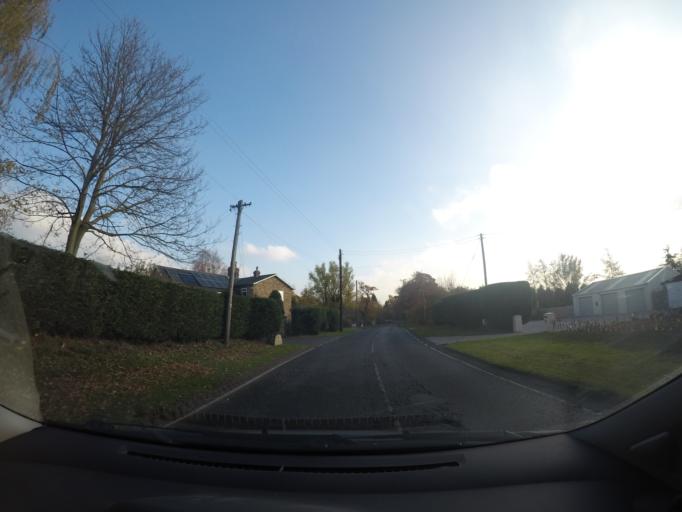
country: GB
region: England
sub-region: City of York
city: Huntington
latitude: 53.9992
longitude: -1.0195
